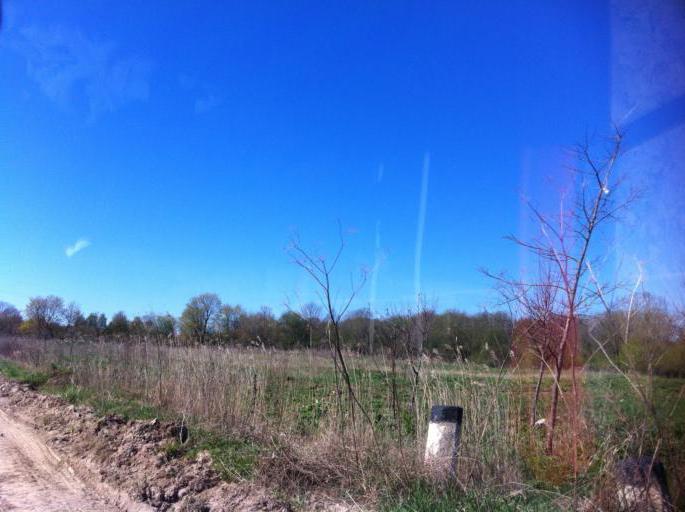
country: RU
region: Pskov
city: Izborsk
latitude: 57.8089
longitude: 27.9792
